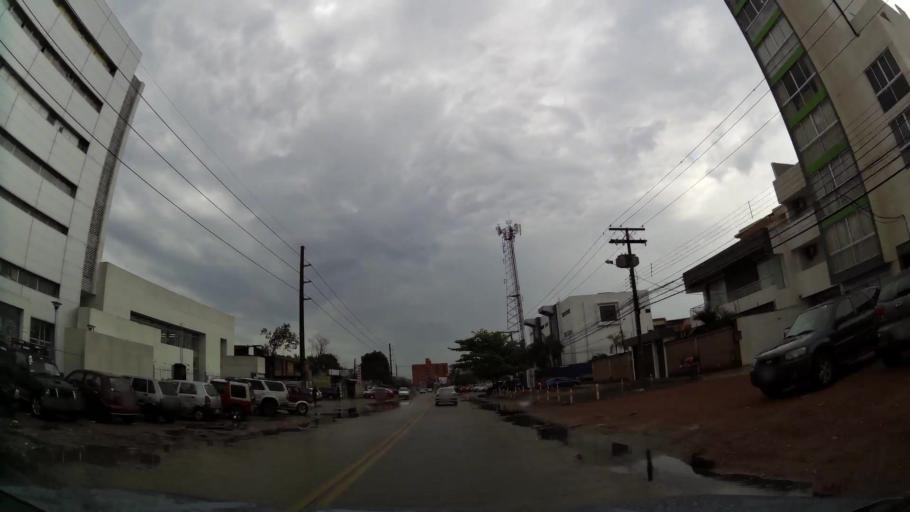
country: BO
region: Santa Cruz
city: Santa Cruz de la Sierra
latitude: -17.7669
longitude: -63.1570
